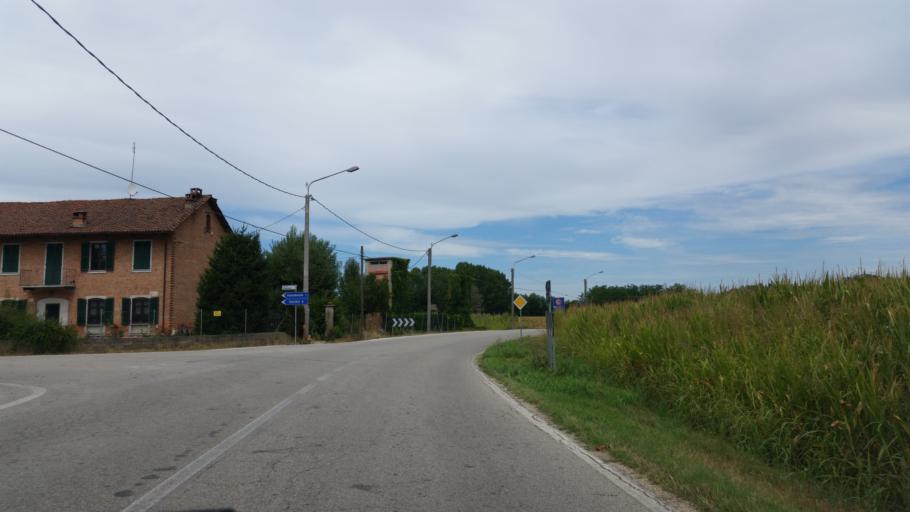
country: IT
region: Piedmont
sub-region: Provincia di Asti
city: Celle Enomondo
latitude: 44.8710
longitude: 8.1133
